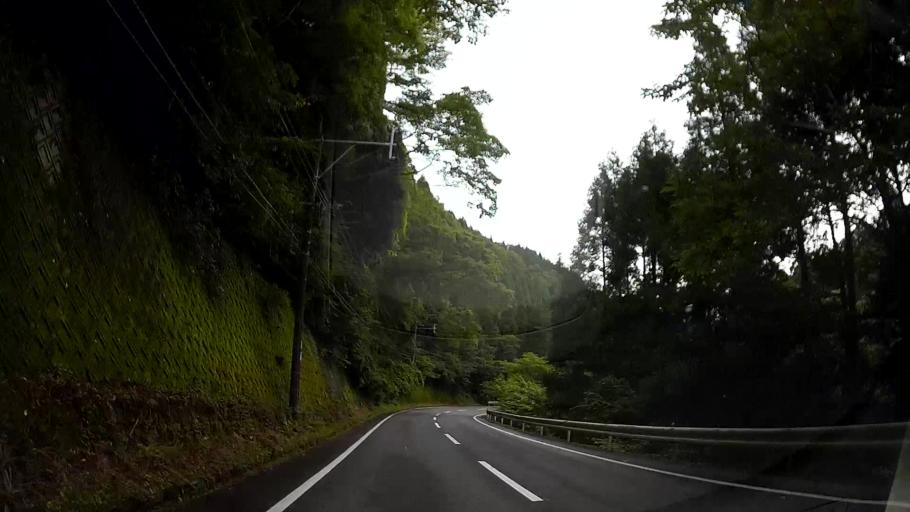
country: JP
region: Kumamoto
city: Kikuchi
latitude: 33.0783
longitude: 130.9323
